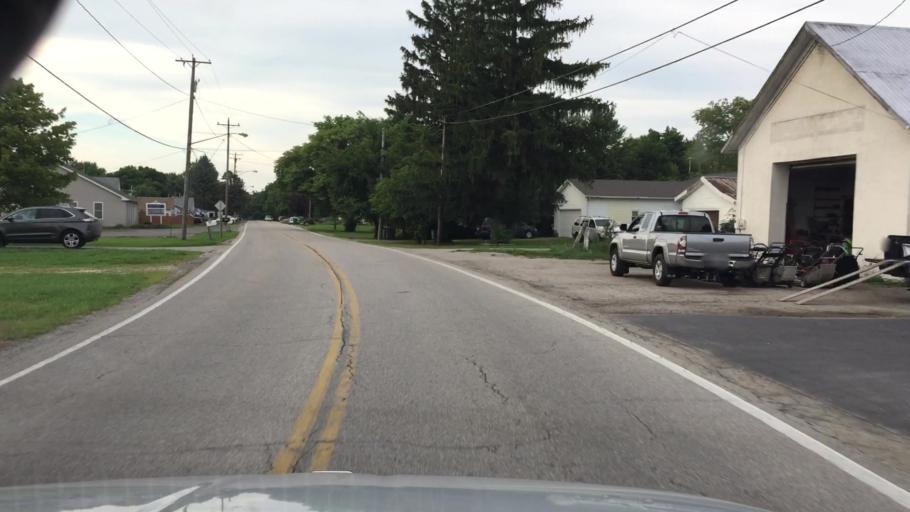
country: US
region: Ohio
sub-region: Madison County
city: Plain City
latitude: 40.0643
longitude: -83.2514
